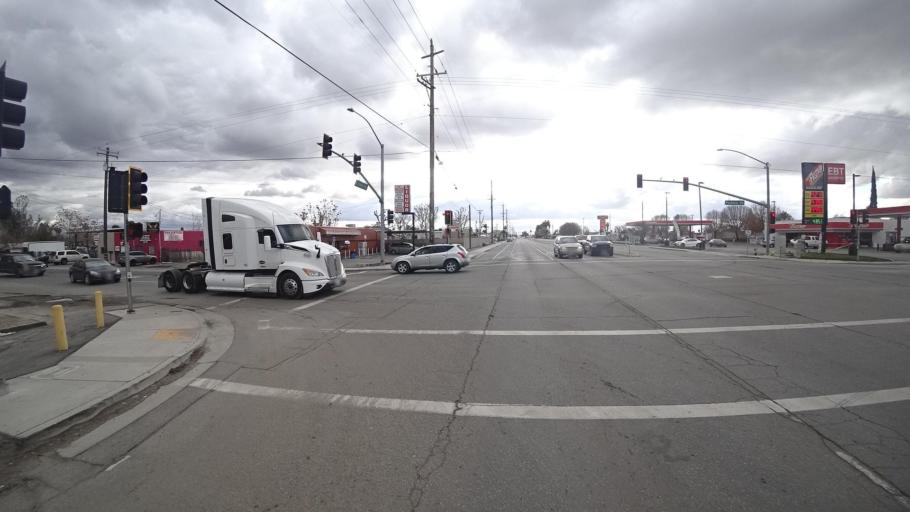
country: US
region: California
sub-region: Kern County
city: Greenfield
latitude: 35.3106
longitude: -119.0029
